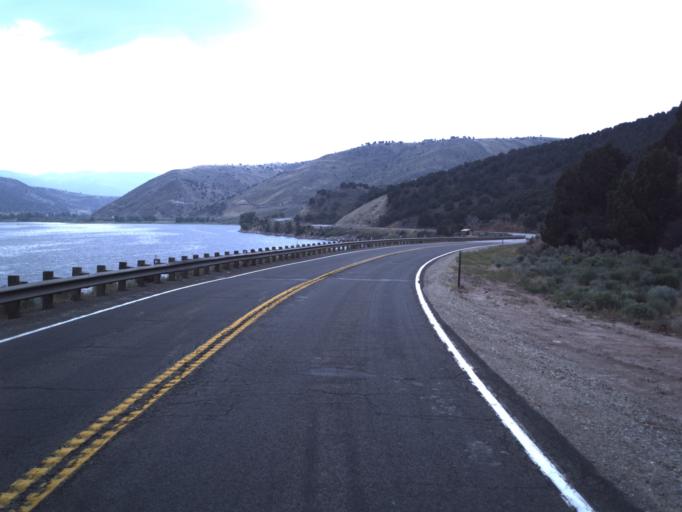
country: US
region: Utah
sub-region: Summit County
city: Oakley
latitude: 40.7661
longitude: -111.3992
